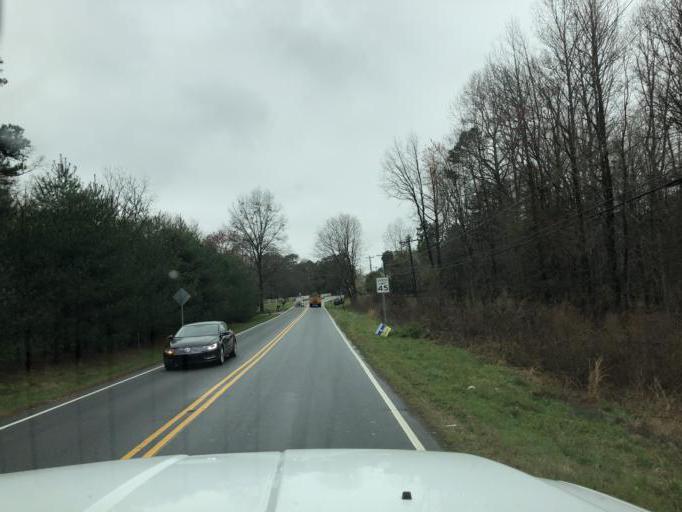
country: US
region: North Carolina
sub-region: Mecklenburg County
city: Huntersville
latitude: 35.3358
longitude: -80.9152
